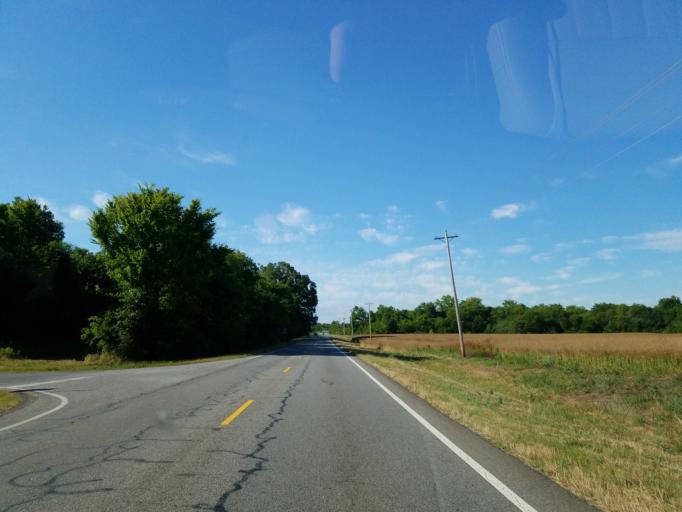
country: US
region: Georgia
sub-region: Bartow County
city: Adairsville
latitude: 34.4167
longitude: -84.9357
